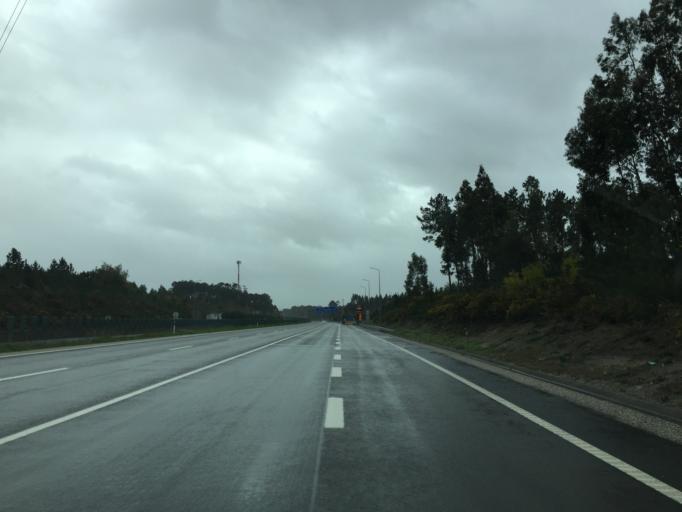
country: PT
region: Leiria
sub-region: Leiria
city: Monte Redondo
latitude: 39.9111
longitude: -8.8003
